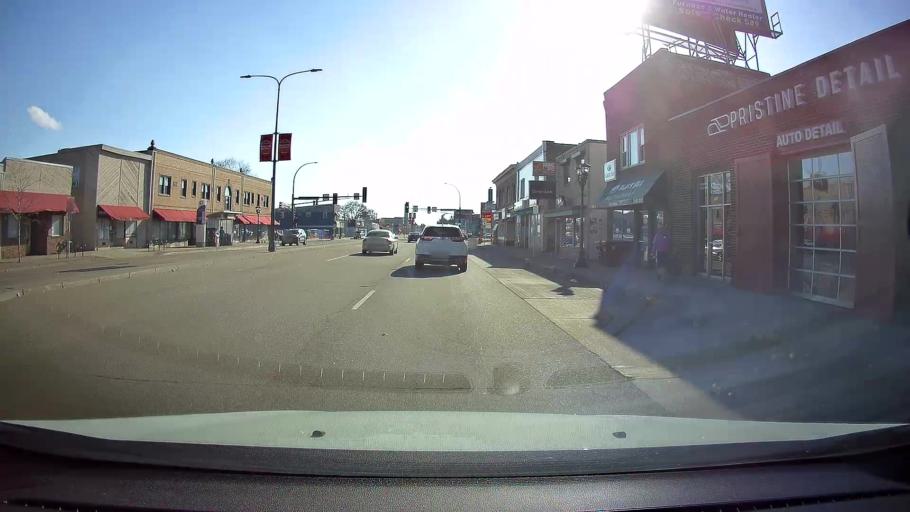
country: US
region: Minnesota
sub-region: Ramsey County
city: Falcon Heights
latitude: 44.9637
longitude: -93.1672
